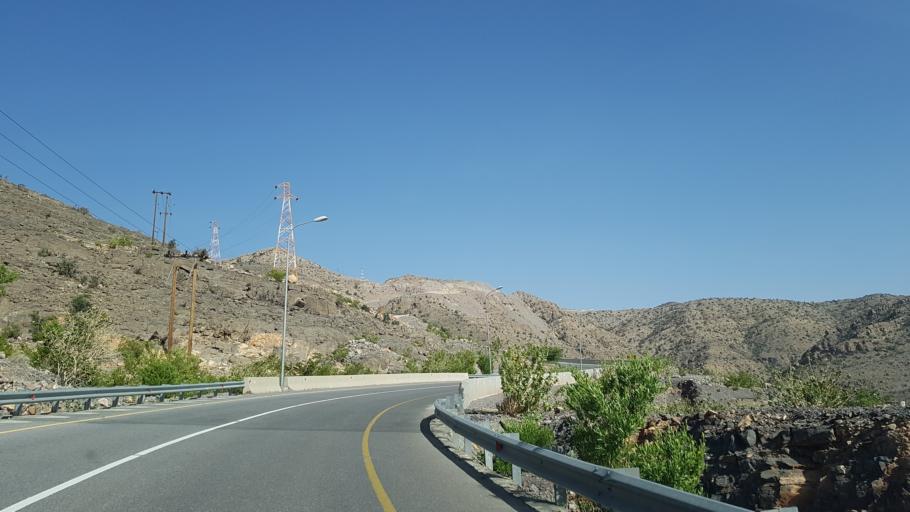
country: OM
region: Muhafazat ad Dakhiliyah
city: Izki
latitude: 23.0665
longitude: 57.7164
